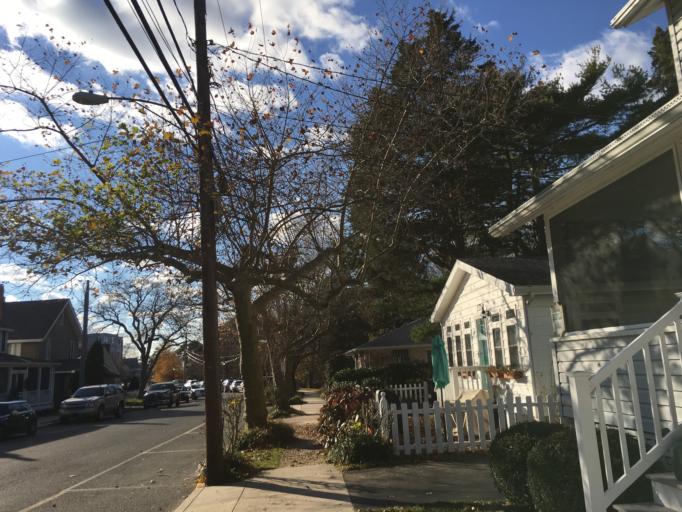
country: US
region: Delaware
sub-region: Sussex County
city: Rehoboth Beach
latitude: 38.7186
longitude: -75.0808
